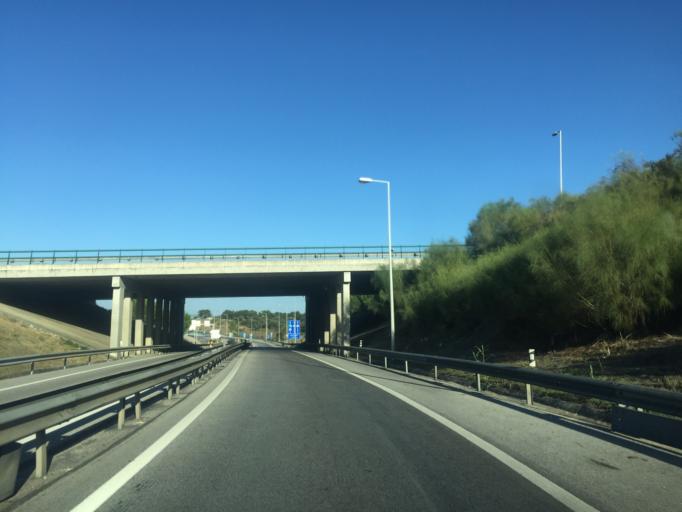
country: PT
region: Lisbon
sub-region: Azambuja
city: Aveiras de Cima
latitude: 39.1404
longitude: -8.8876
